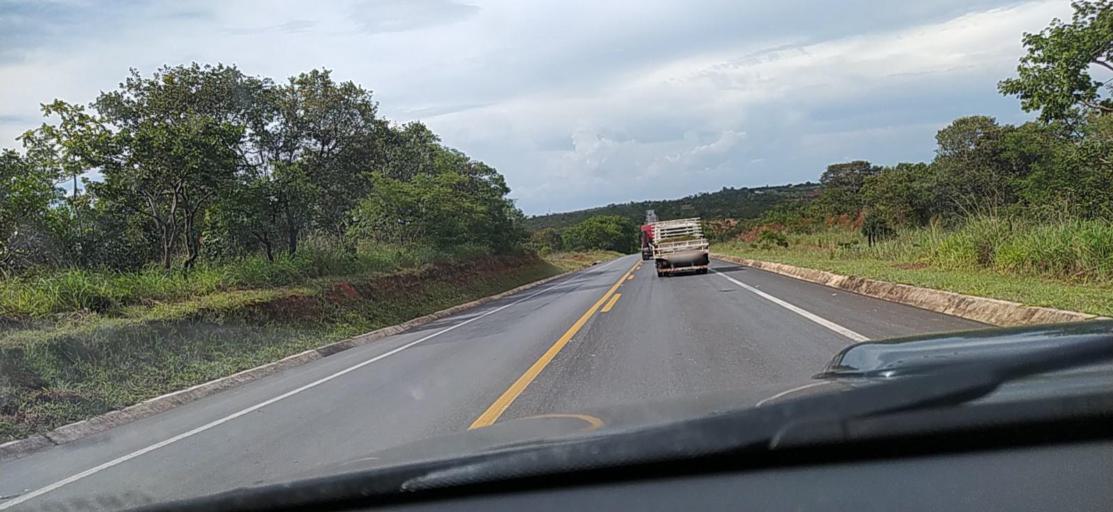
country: BR
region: Minas Gerais
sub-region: Montes Claros
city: Montes Claros
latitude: -16.8591
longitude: -43.8532
